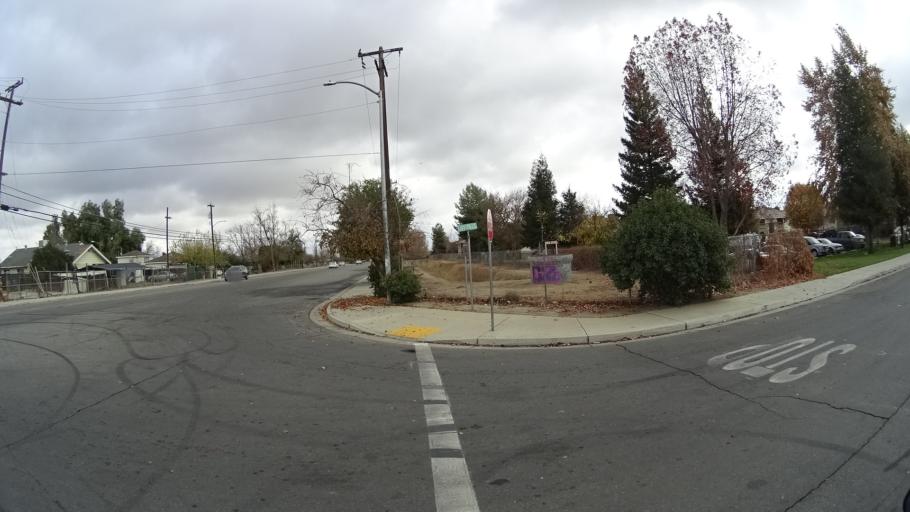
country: US
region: California
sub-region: Kern County
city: Bakersfield
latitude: 35.3394
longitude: -118.9899
